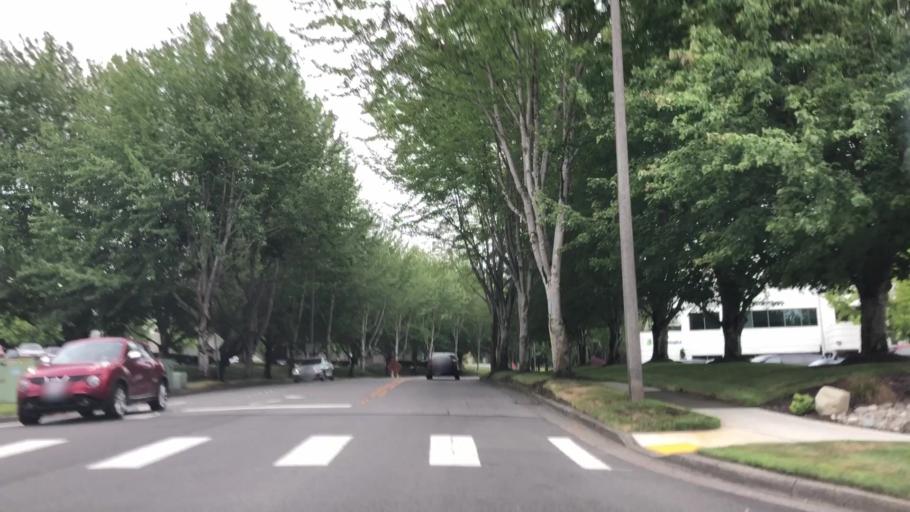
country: US
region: Washington
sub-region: Snohomish County
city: North Creek
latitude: 47.7991
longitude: -122.2060
